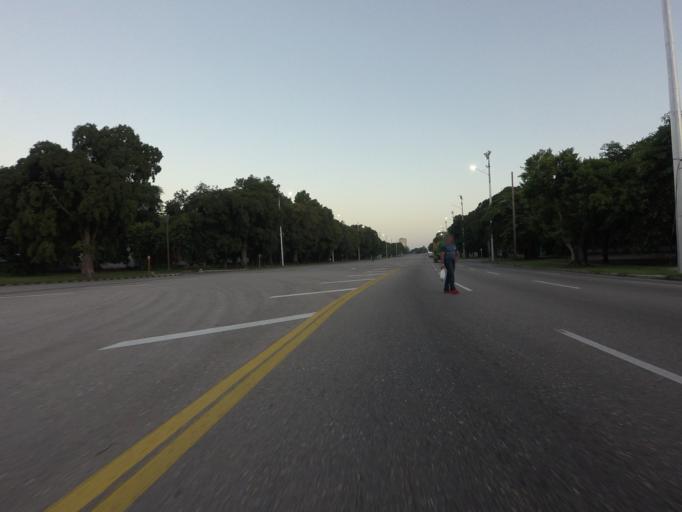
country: CU
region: La Habana
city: Havana
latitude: 23.1246
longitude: -82.3882
